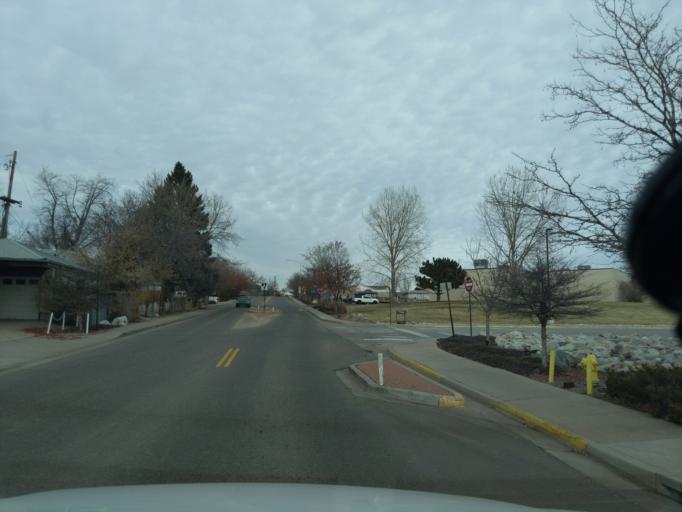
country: US
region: Colorado
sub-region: Adams County
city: Thornton
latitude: 39.8583
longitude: -104.9591
